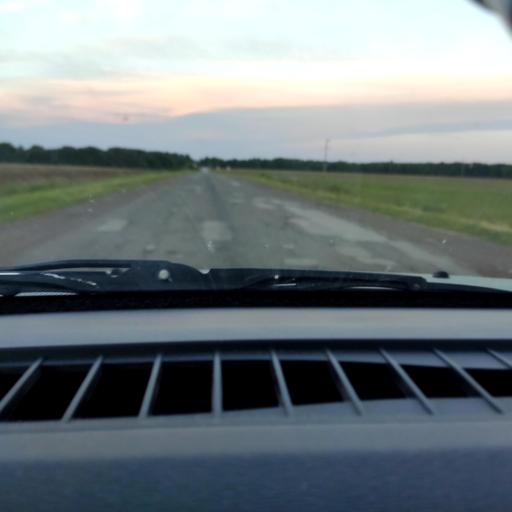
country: RU
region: Perm
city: Uinskoye
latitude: 57.2329
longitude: 56.5444
